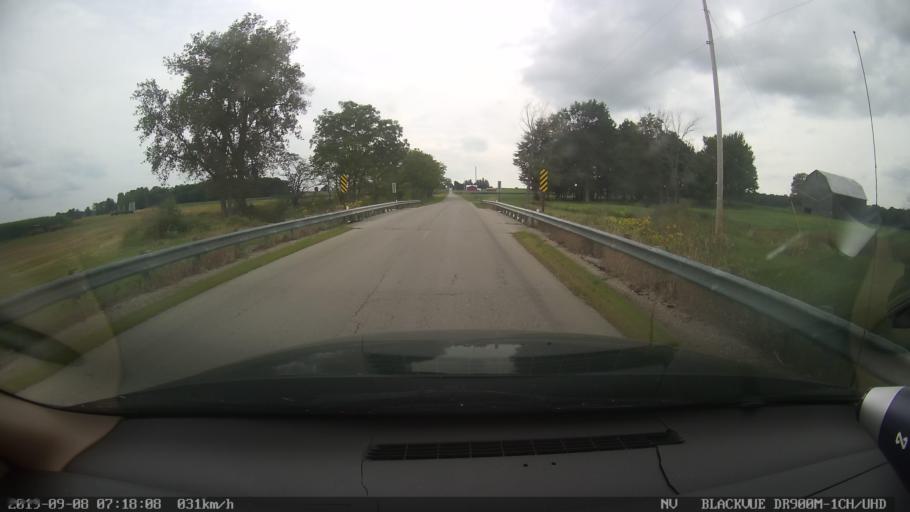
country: US
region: Ohio
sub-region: Richland County
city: Shelby
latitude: 40.9087
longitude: -82.7221
